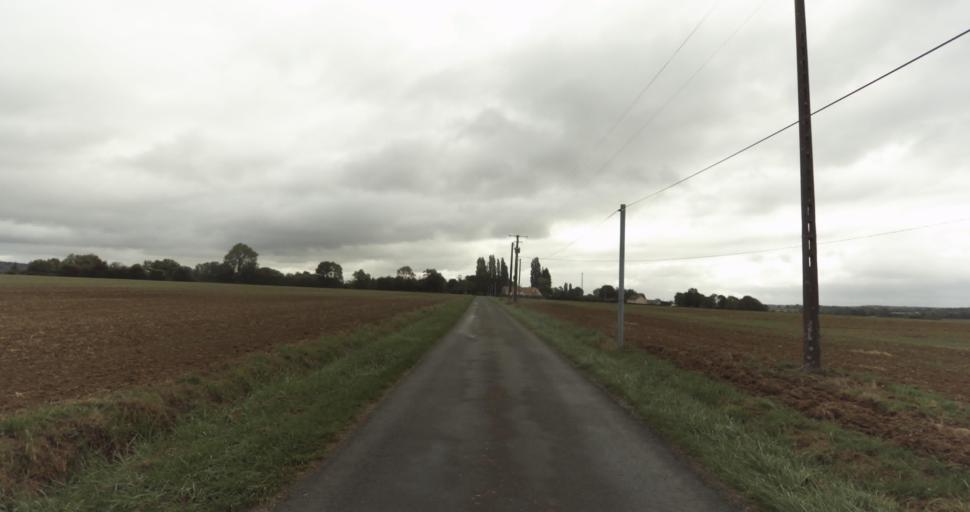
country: FR
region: Lower Normandy
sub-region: Departement de l'Orne
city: Sainte-Gauburge-Sainte-Colombe
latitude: 48.7278
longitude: 0.4360
